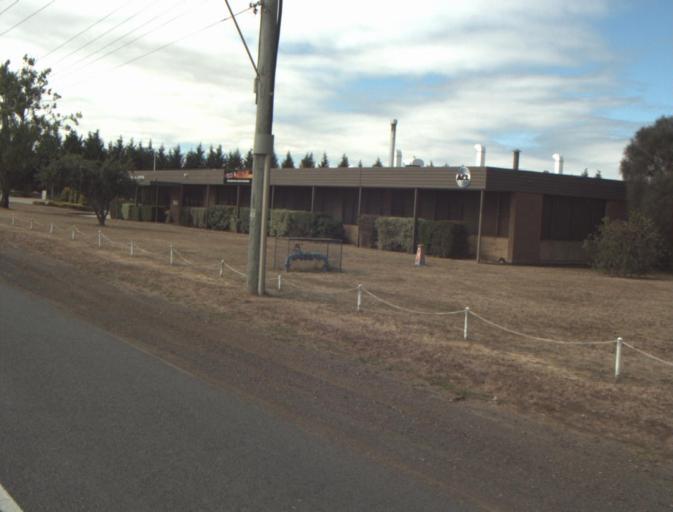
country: AU
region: Tasmania
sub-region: Launceston
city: Mayfield
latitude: -41.3749
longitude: 147.1203
